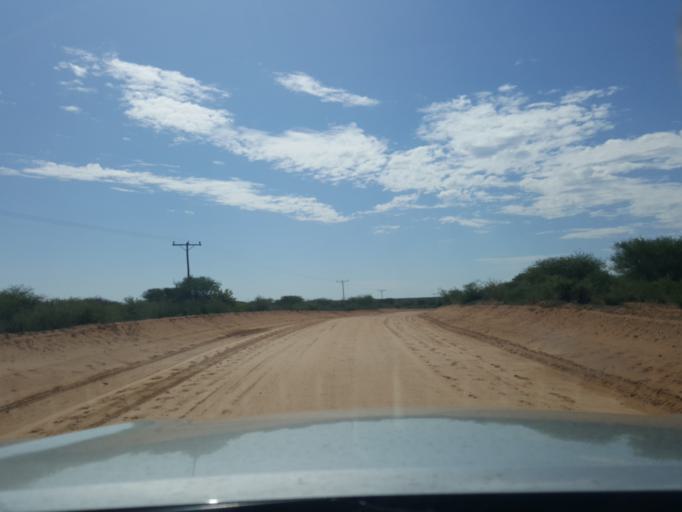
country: BW
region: Kweneng
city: Khudumelapye
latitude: -23.8865
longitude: 24.9131
